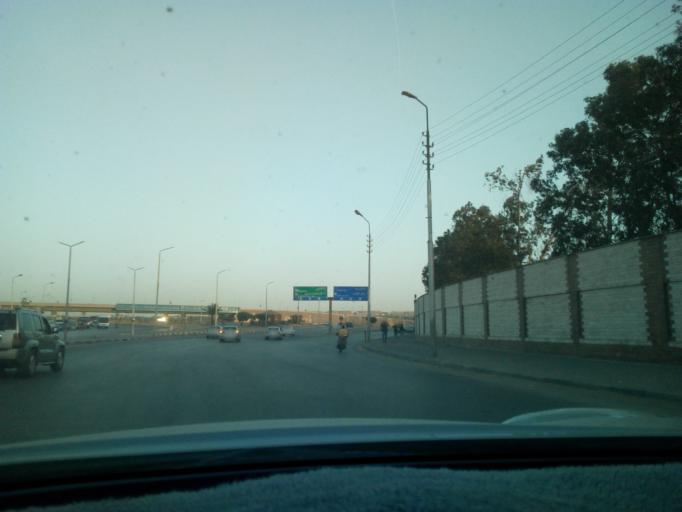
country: EG
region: Muhafazat al Qalyubiyah
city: Al Khankah
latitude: 30.1169
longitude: 31.3635
